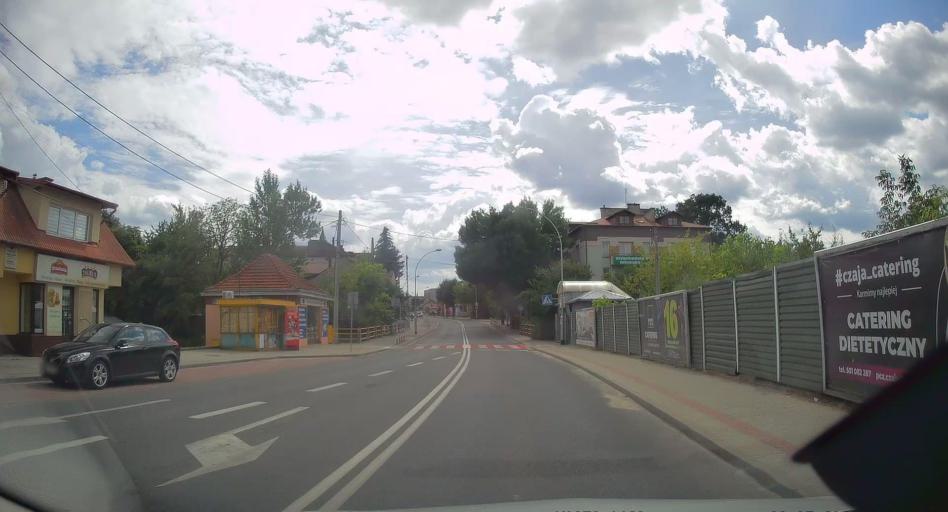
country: PL
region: Subcarpathian Voivodeship
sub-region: Powiat debicki
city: Debica
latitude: 50.0499
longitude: 21.4084
